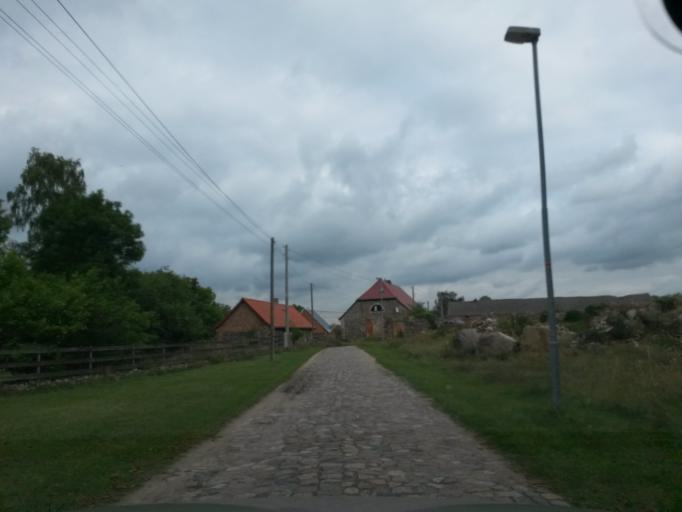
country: DE
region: Brandenburg
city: Gerswalde
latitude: 53.0921
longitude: 13.8419
